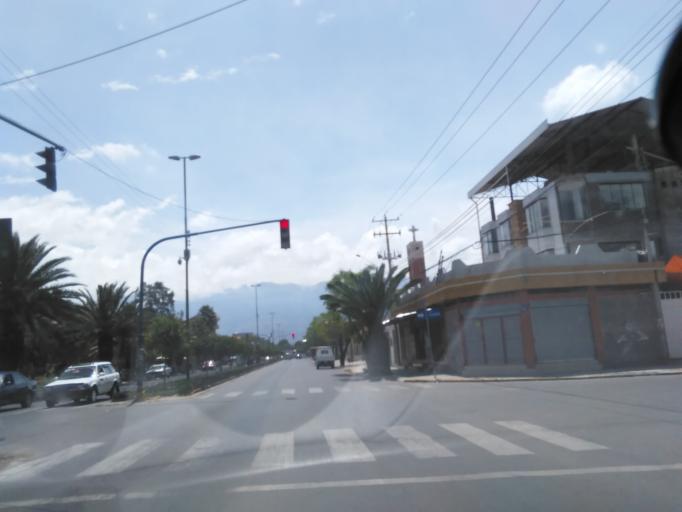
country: BO
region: Cochabamba
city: Cochabamba
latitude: -17.4151
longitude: -66.1654
